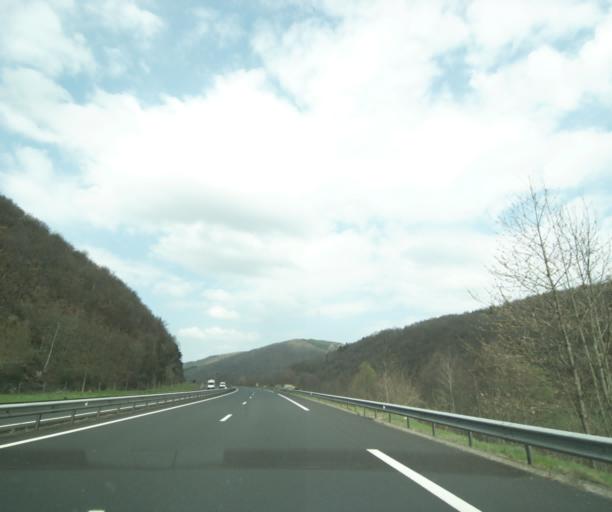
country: FR
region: Auvergne
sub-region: Departement du Cantal
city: Massiac
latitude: 45.2245
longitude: 3.2069
